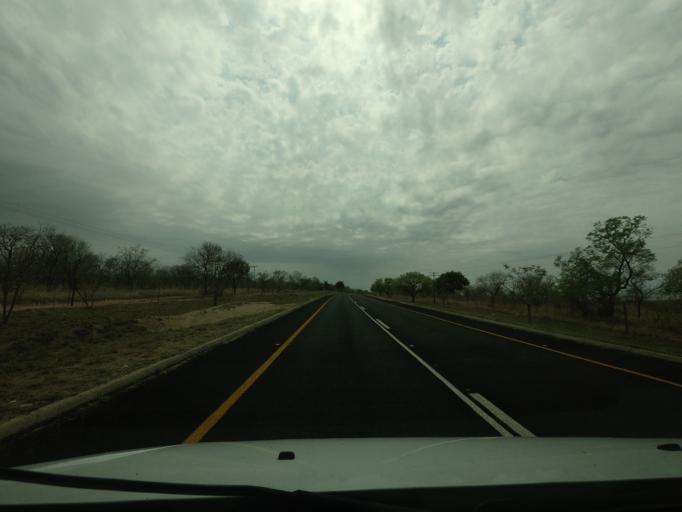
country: ZA
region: Limpopo
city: Thulamahashi
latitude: -24.5559
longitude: 31.1809
